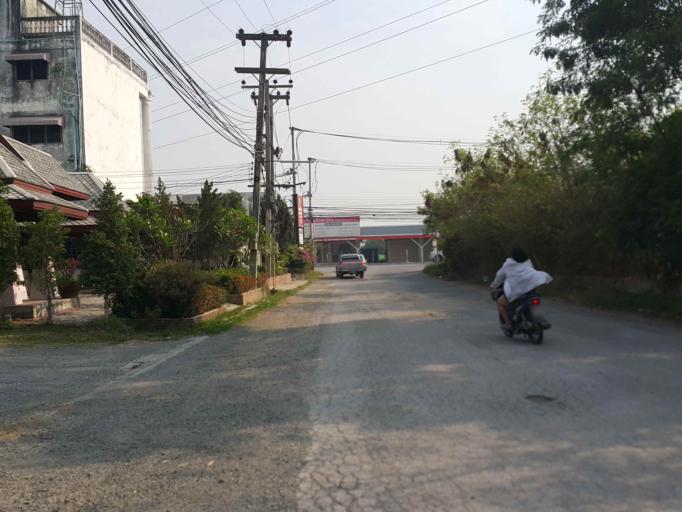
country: TH
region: Chiang Mai
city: San Kamphaeng
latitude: 18.7738
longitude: 99.0615
